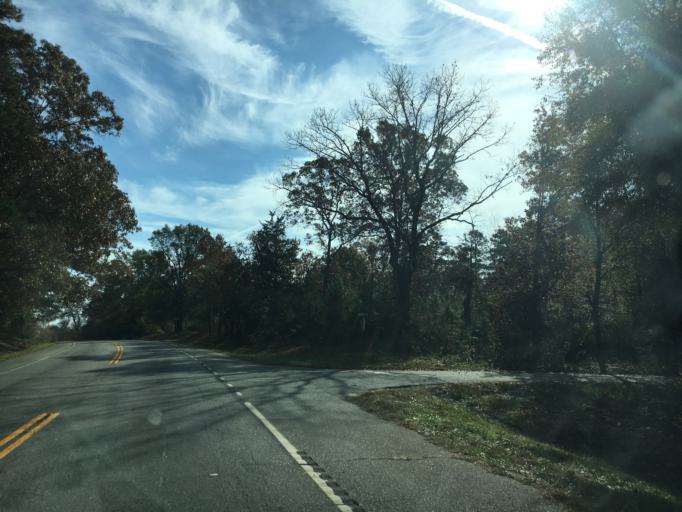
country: US
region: South Carolina
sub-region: Anderson County
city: Belton
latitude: 34.5774
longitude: -82.5529
